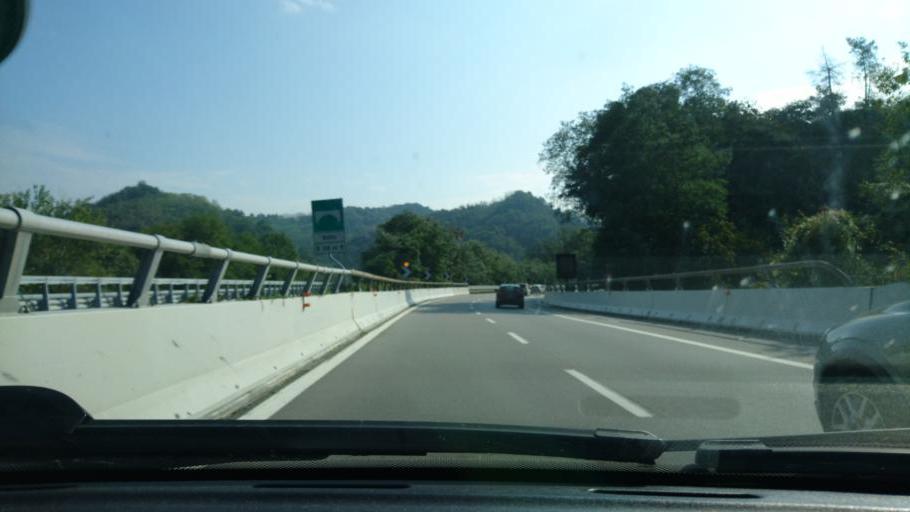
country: IT
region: Liguria
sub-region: Provincia di Savona
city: Quiliano
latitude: 44.3216
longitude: 8.3789
